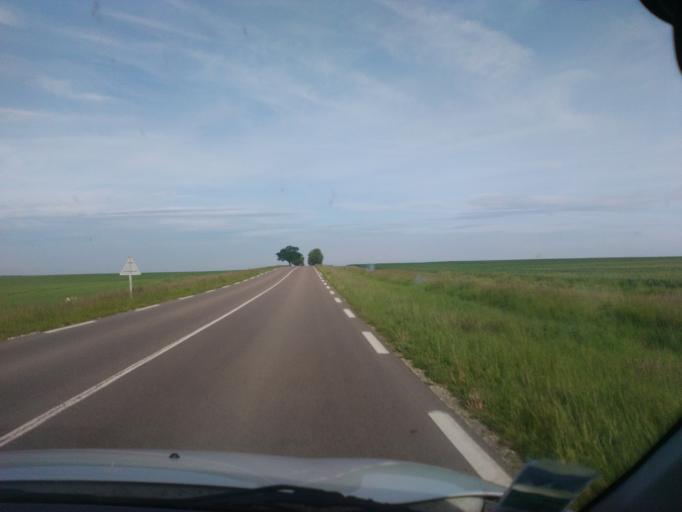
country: FR
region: Champagne-Ardenne
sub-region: Departement de l'Aube
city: Vendeuvre-sur-Barse
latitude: 48.2355
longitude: 4.5142
